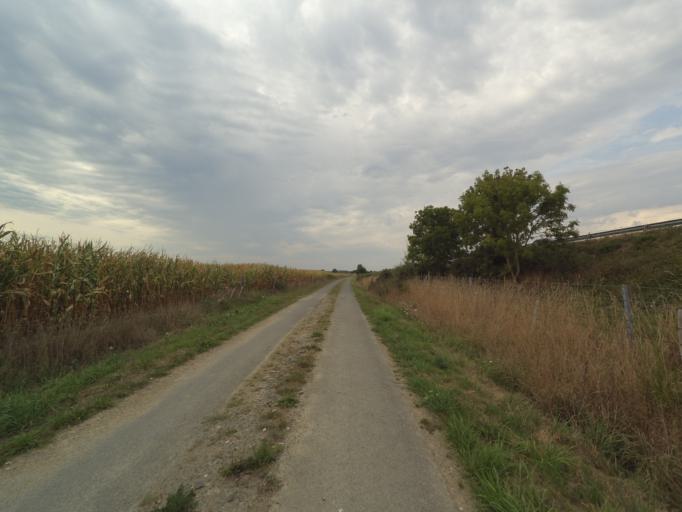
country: FR
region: Pays de la Loire
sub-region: Departement de la Vendee
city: Bouffere
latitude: 46.9862
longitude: -1.3799
